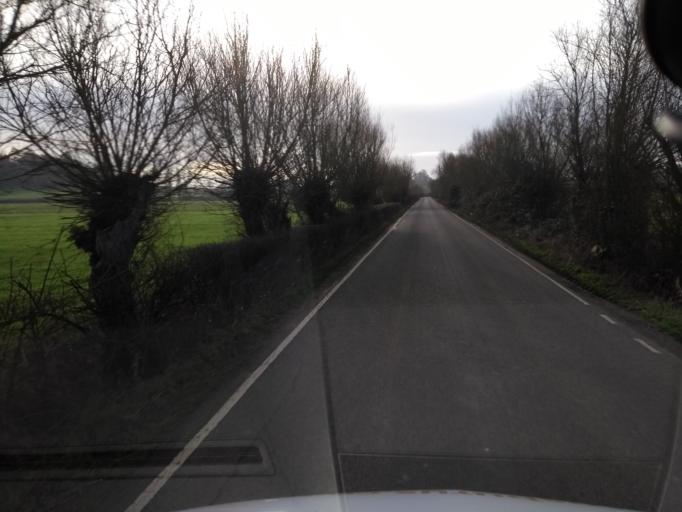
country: GB
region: England
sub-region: Somerset
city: Creech Saint Michael
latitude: 51.0340
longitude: -2.9749
